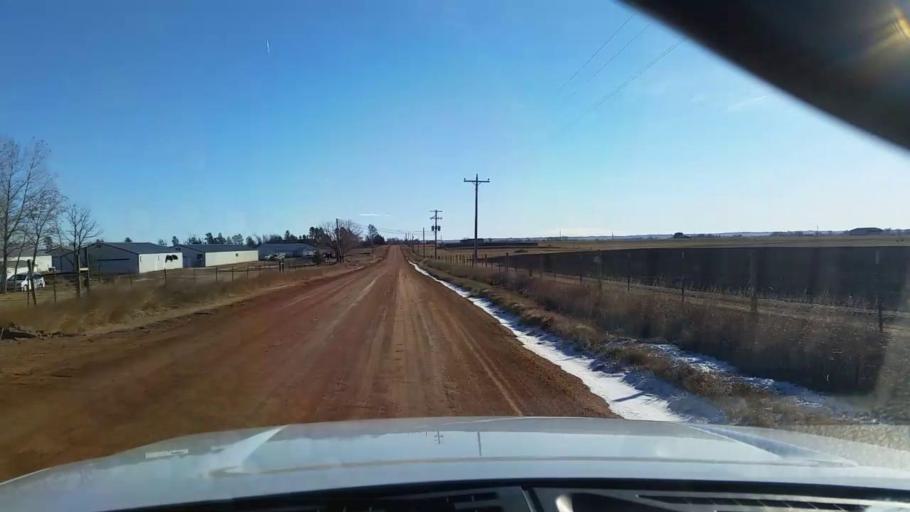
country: US
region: Colorado
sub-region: Larimer County
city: Wellington
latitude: 40.7695
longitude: -105.0721
